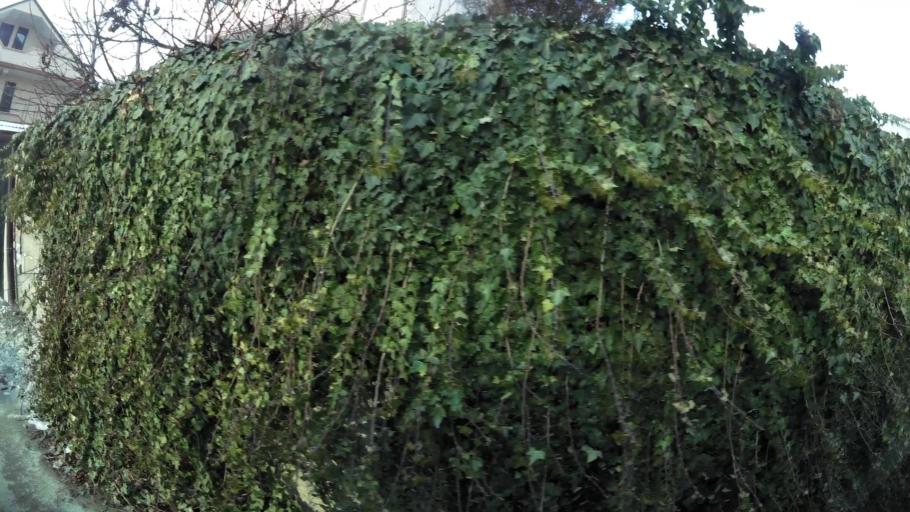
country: MK
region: Cair
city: Cair
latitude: 42.0148
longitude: 21.4429
